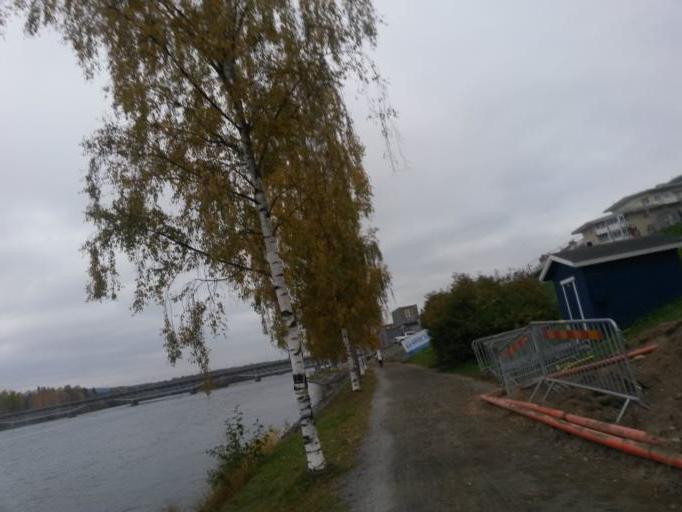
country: SE
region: Vaesterbotten
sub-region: Skelleftea Kommun
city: Skelleftea
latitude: 64.7482
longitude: 20.9570
